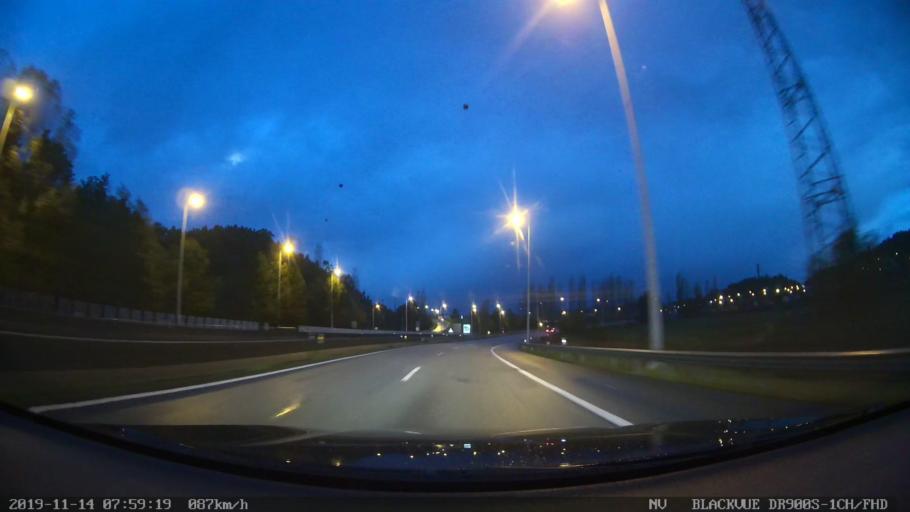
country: PT
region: Braga
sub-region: Braga
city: Oliveira
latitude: 41.5053
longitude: -8.4443
